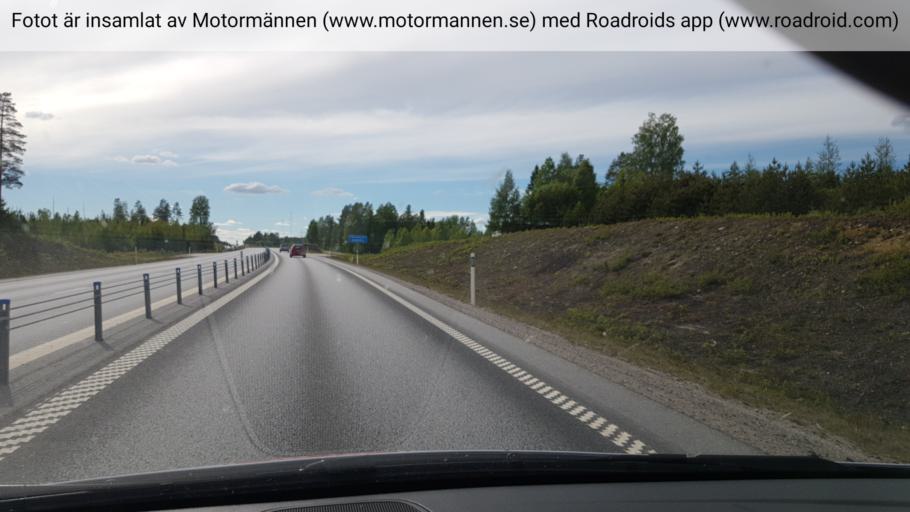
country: SE
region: Vaesterbotten
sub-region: Vannas Kommun
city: Vannasby
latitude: 63.8941
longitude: 19.9702
